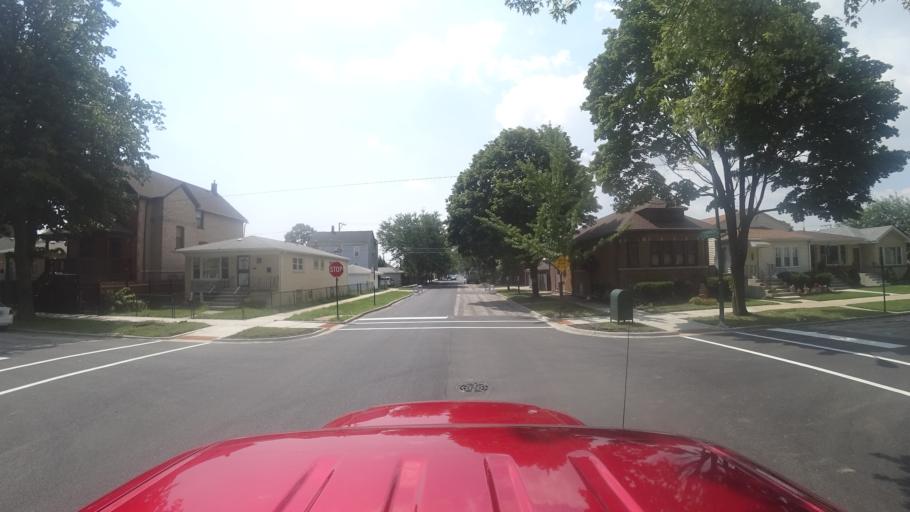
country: US
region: Illinois
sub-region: Cook County
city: Hometown
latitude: 41.7907
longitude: -87.7157
